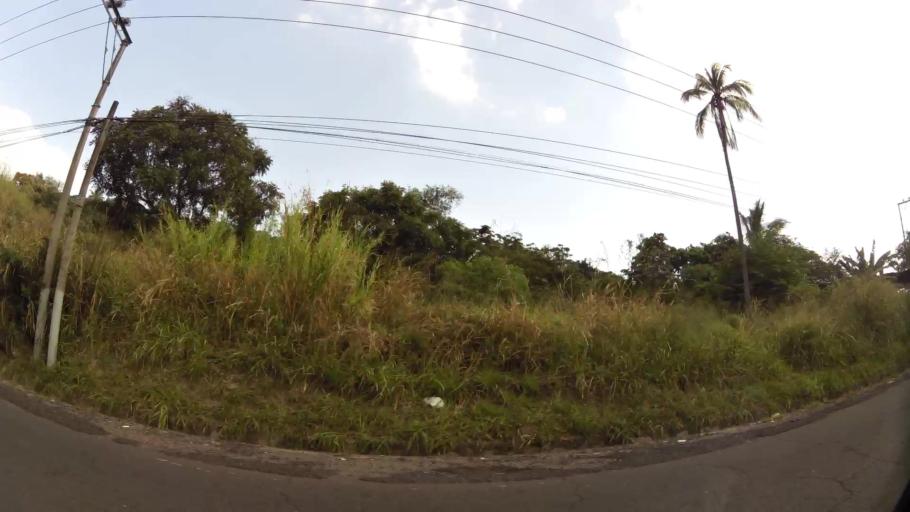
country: SV
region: San Salvador
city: Delgado
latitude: 13.7186
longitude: -89.1568
